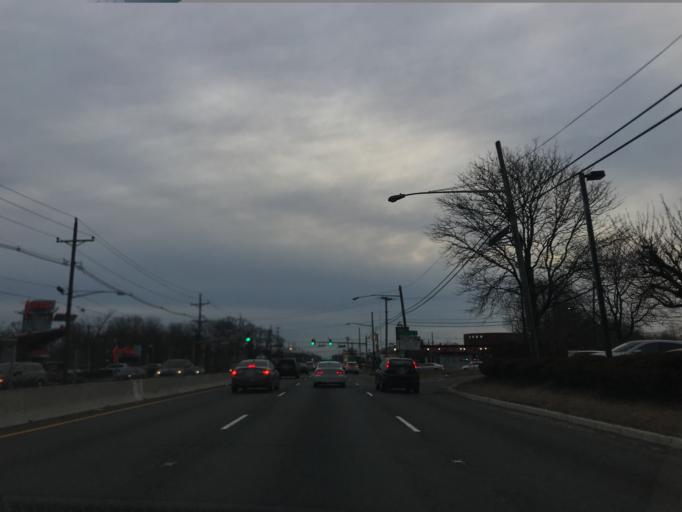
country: US
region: New Jersey
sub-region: Middlesex County
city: Piscataway
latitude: 40.5085
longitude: -74.3907
